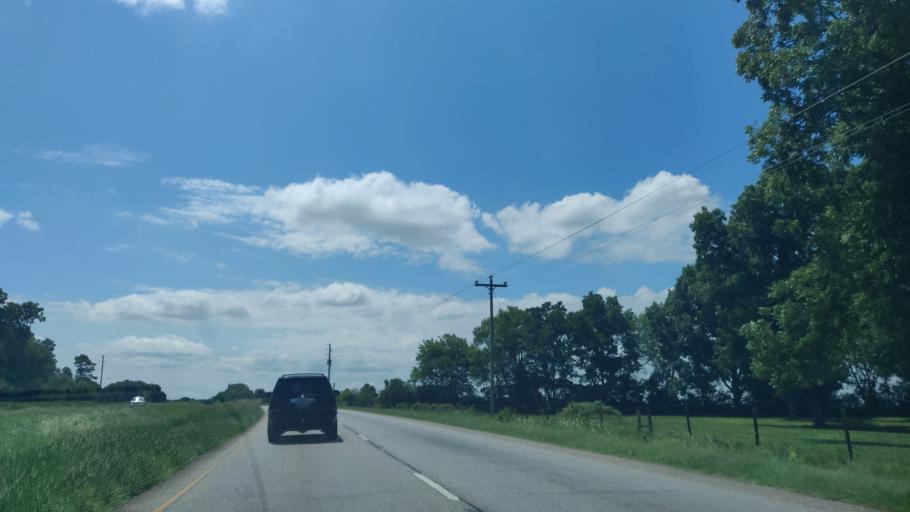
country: US
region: Georgia
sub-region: Stewart County
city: Richland
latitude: 32.0133
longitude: -84.6584
